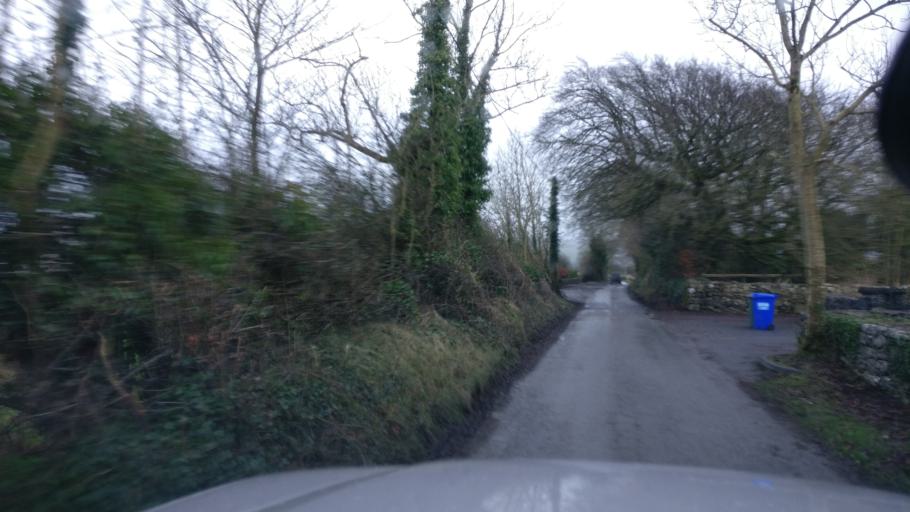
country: IE
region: Connaught
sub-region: County Galway
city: Loughrea
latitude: 53.1962
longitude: -8.6632
